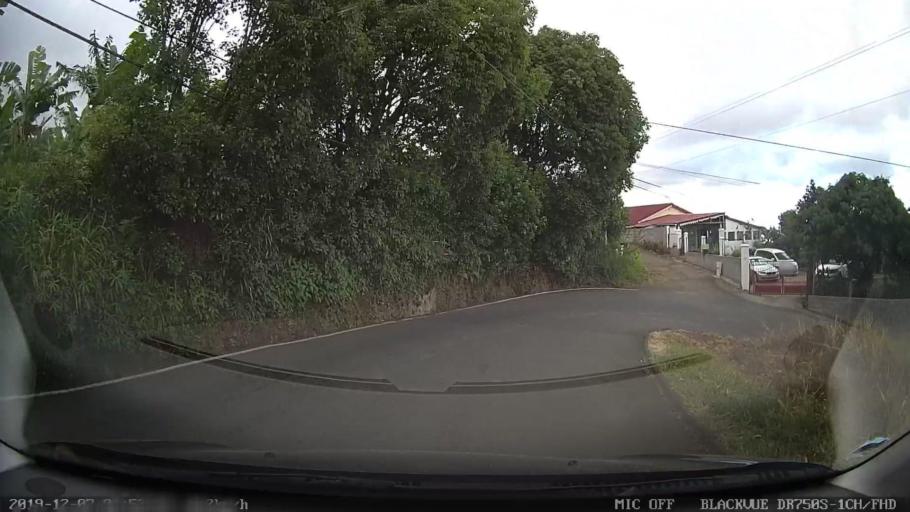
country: RE
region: Reunion
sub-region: Reunion
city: Sainte-Marie
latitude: -20.9390
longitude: 55.5336
